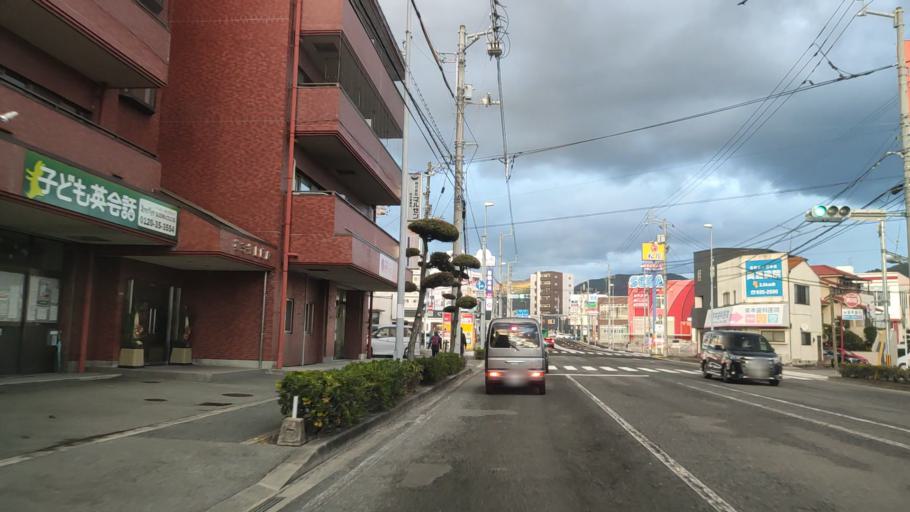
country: JP
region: Ehime
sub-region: Shikoku-chuo Shi
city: Matsuyama
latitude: 33.8278
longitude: 132.7851
